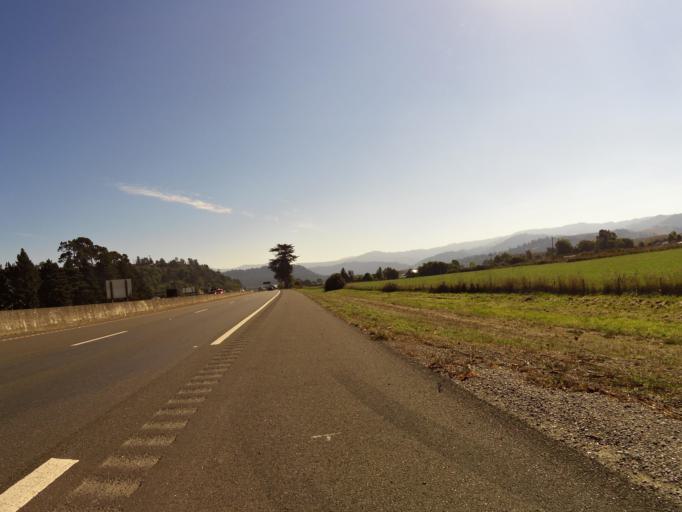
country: US
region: California
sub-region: Humboldt County
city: Fortuna
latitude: 40.5667
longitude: -124.1478
